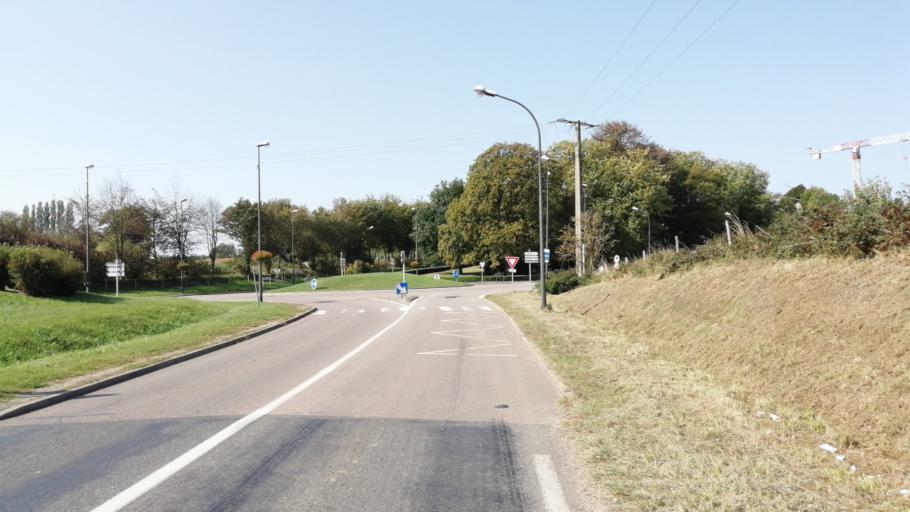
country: FR
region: Haute-Normandie
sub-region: Departement de la Seine-Maritime
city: Saint-Romain-de-Colbosc
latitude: 49.5243
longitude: 0.3676
